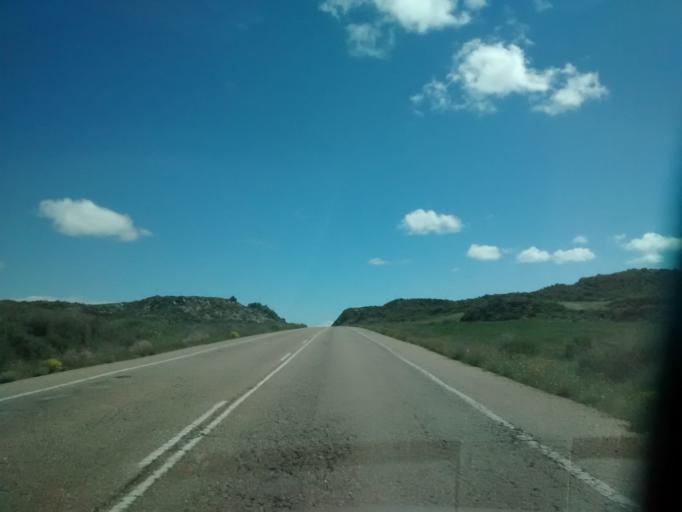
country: ES
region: Aragon
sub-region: Provincia de Zaragoza
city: Lecinena
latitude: 41.8023
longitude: -0.6021
